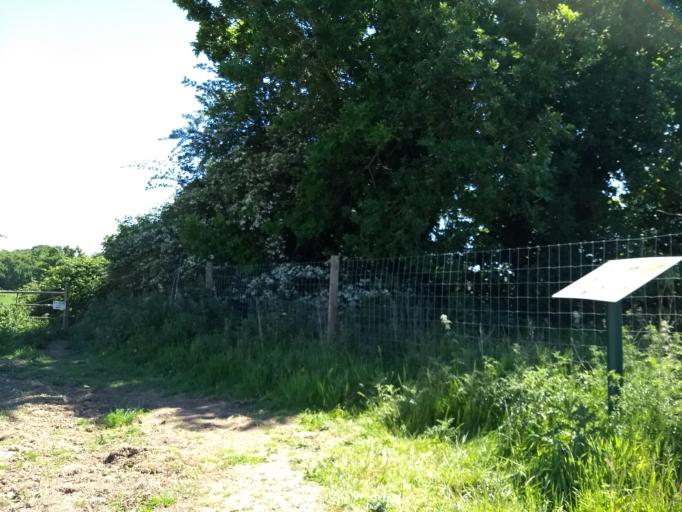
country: GB
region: England
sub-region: Isle of Wight
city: Seaview
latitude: 50.6998
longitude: -1.1211
